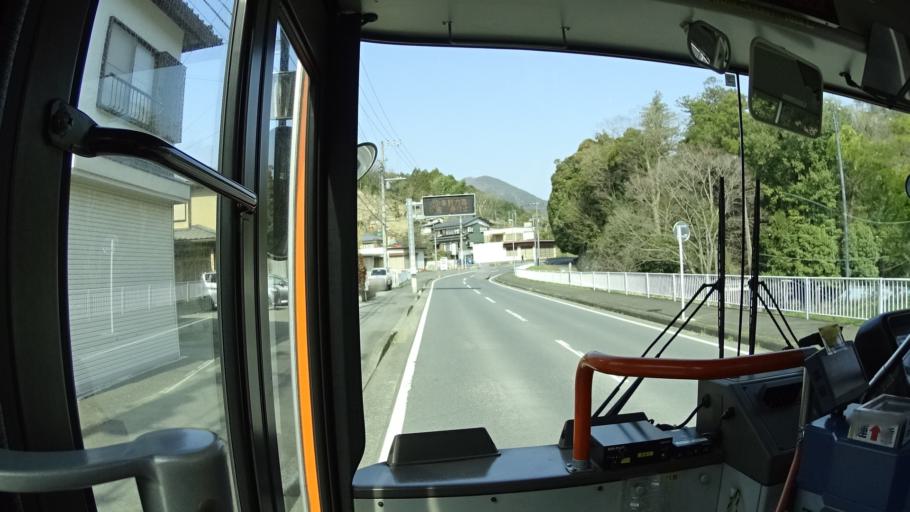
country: JP
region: Kanagawa
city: Atsugi
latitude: 35.4726
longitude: 139.2859
